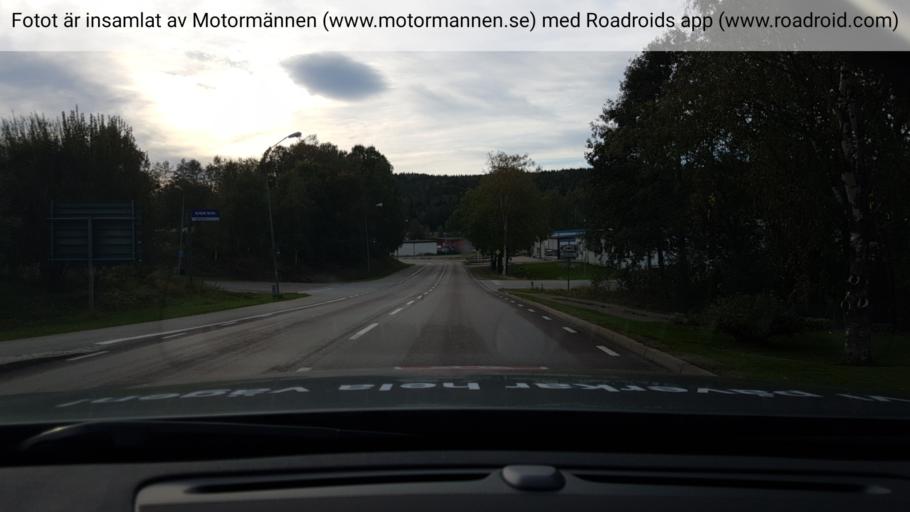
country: SE
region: Vaermland
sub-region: Arjangs Kommun
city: Arjaeng
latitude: 59.3961
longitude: 12.1373
